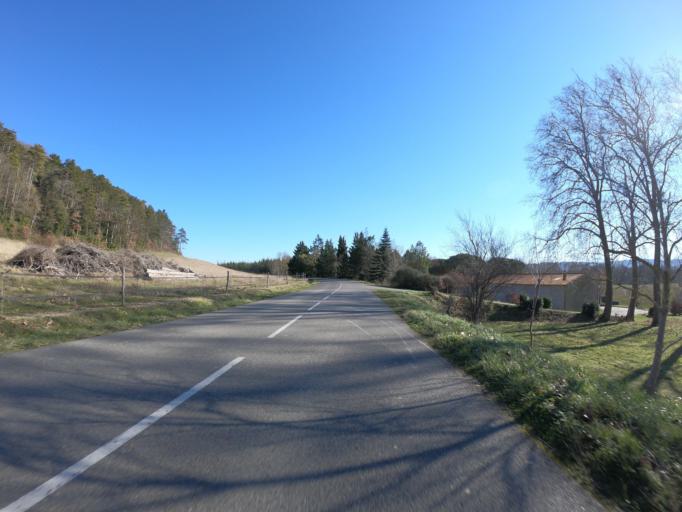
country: FR
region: Midi-Pyrenees
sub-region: Departement de l'Ariege
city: Mirepoix
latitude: 43.0848
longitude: 1.7892
